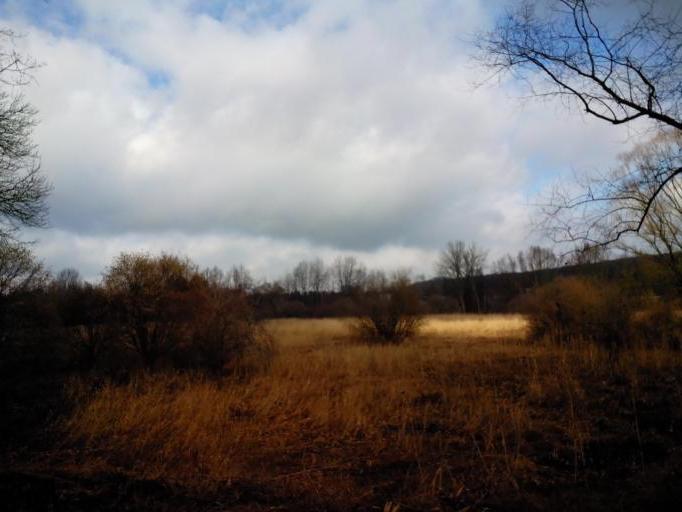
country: BE
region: Wallonia
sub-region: Province du Brabant Wallon
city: Grez-Doiceau
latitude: 50.7557
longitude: 4.6508
